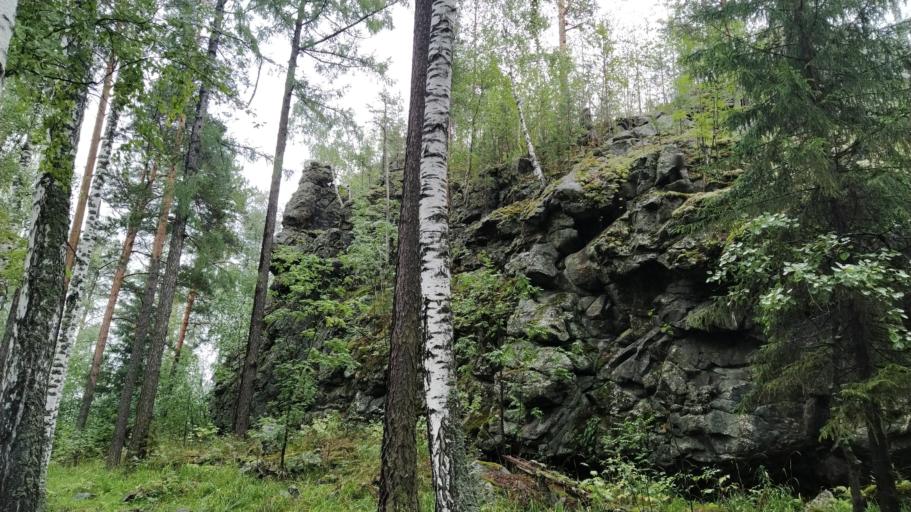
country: RU
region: Sverdlovsk
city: Zyuzel'skiy
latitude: 56.5305
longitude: 59.9846
